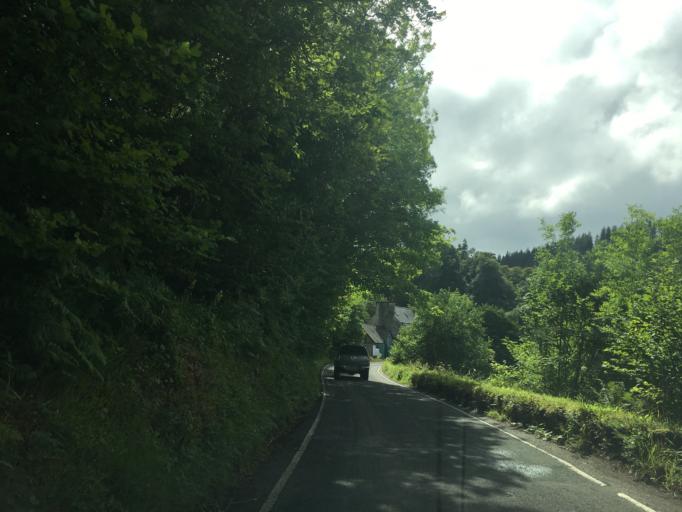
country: GB
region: Scotland
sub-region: Argyll and Bute
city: Ardrishaig
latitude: 56.0755
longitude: -5.5384
